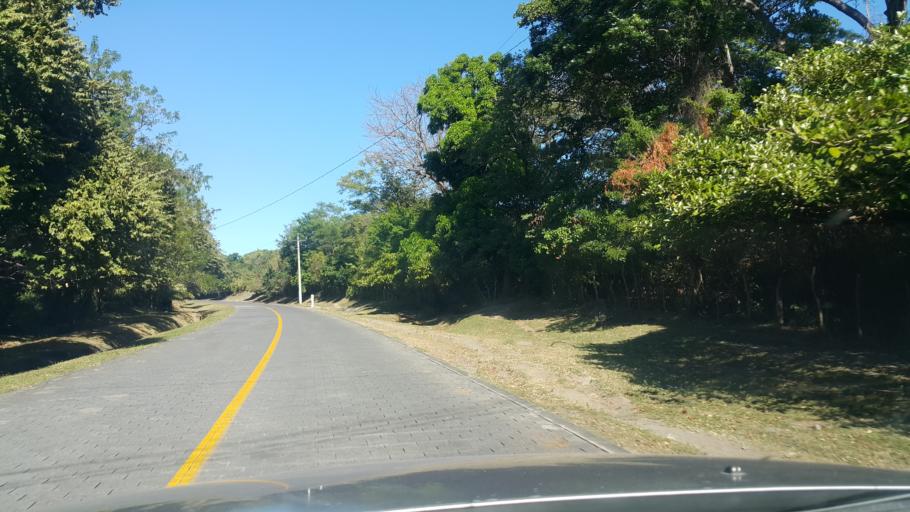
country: NI
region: Rivas
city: Moyogalpa
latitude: 11.4874
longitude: -85.6326
